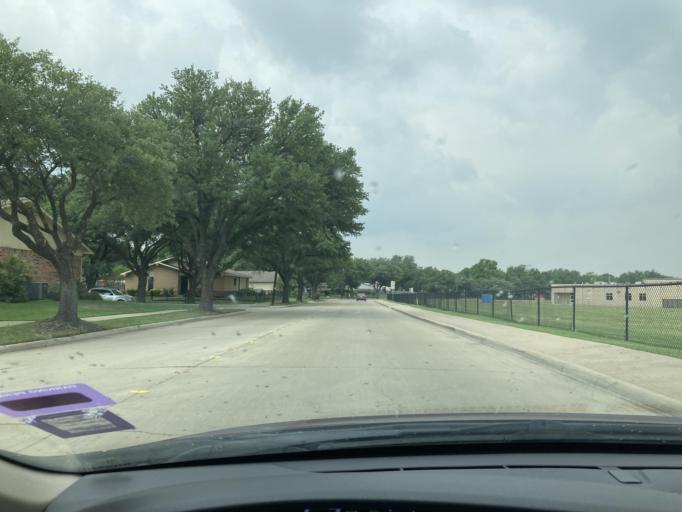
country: US
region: Texas
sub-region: Collin County
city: Plano
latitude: 33.0490
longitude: -96.7215
